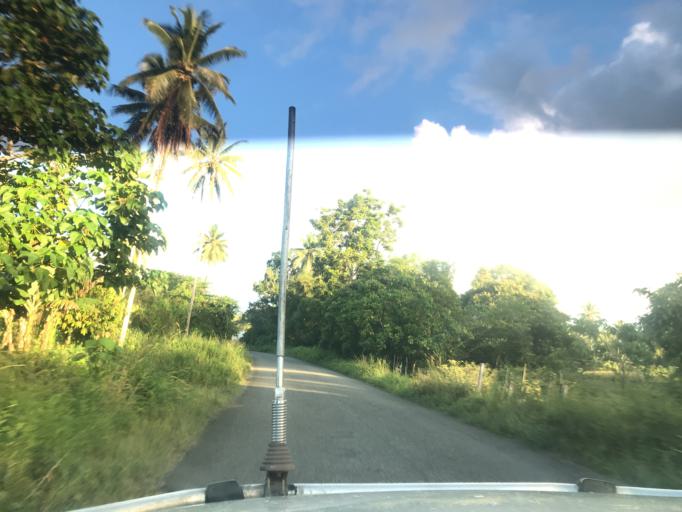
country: SB
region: Malaita
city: Auki
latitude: -8.7226
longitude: 160.7042
